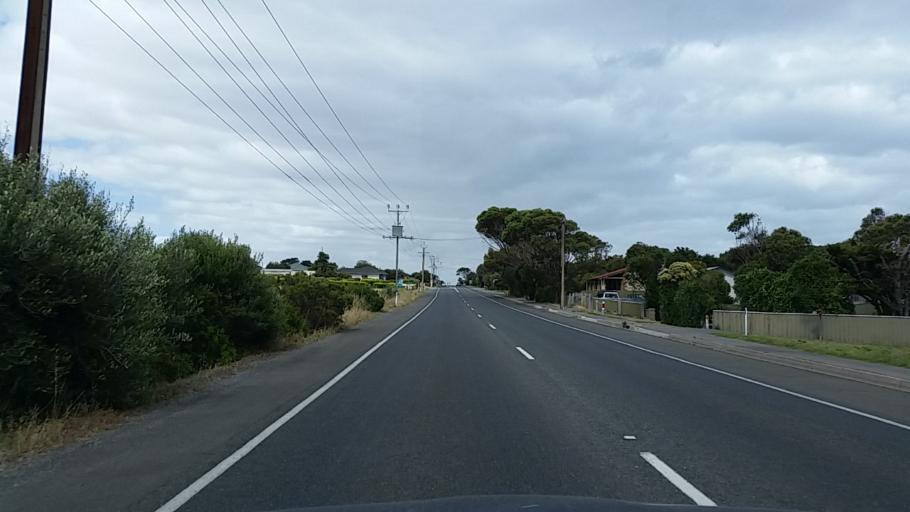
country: AU
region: South Australia
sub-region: Alexandrina
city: Port Elliot
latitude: -35.5320
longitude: 138.6689
